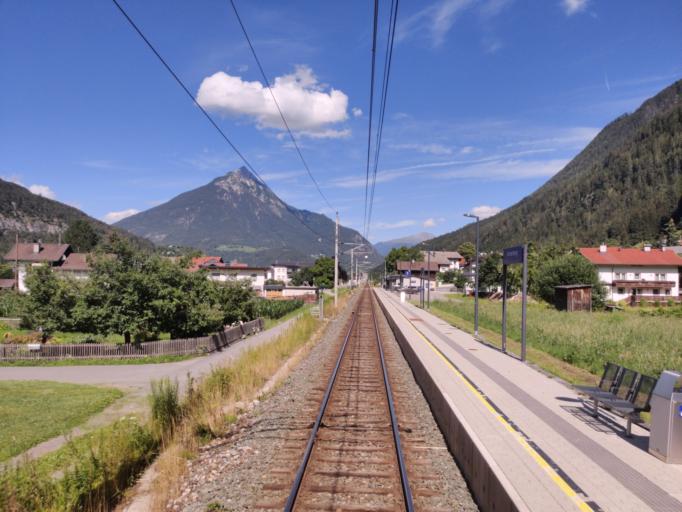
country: AT
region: Tyrol
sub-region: Politischer Bezirk Imst
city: Imsterberg
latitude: 47.2110
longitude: 10.7043
